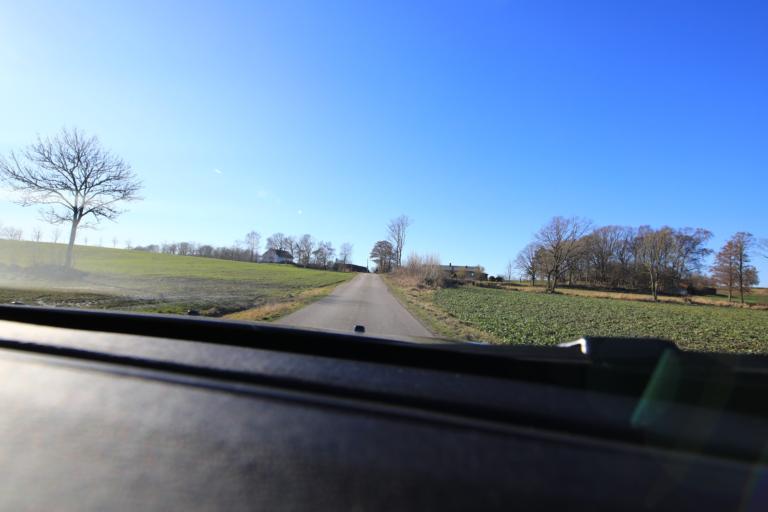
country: SE
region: Halland
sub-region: Varbergs Kommun
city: Tvaaker
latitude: 57.0649
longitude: 12.3950
